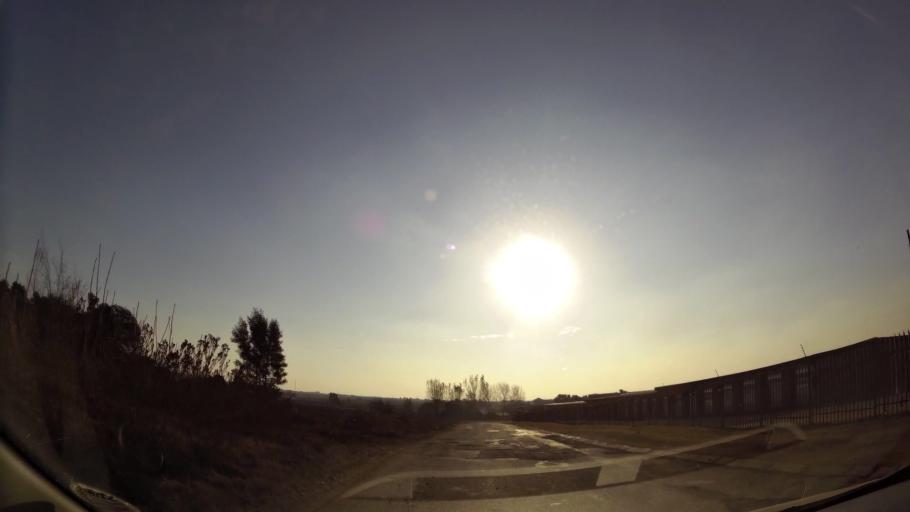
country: ZA
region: Gauteng
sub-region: West Rand District Municipality
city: Randfontein
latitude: -26.2017
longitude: 27.6845
